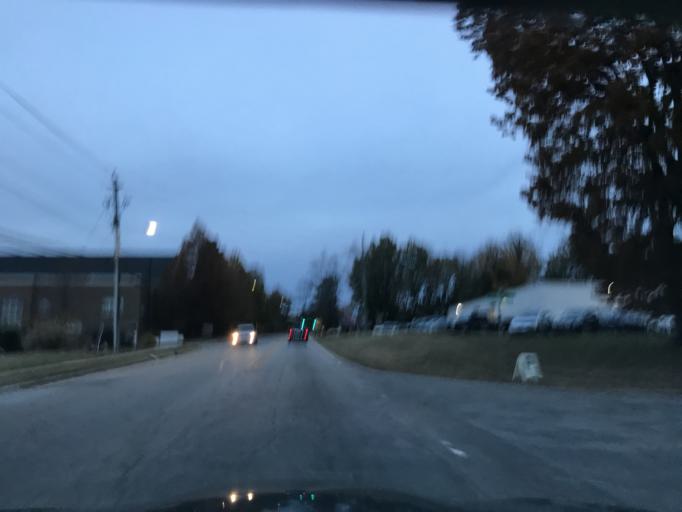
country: US
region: North Carolina
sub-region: Wake County
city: Raleigh
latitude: 35.8483
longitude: -78.6070
